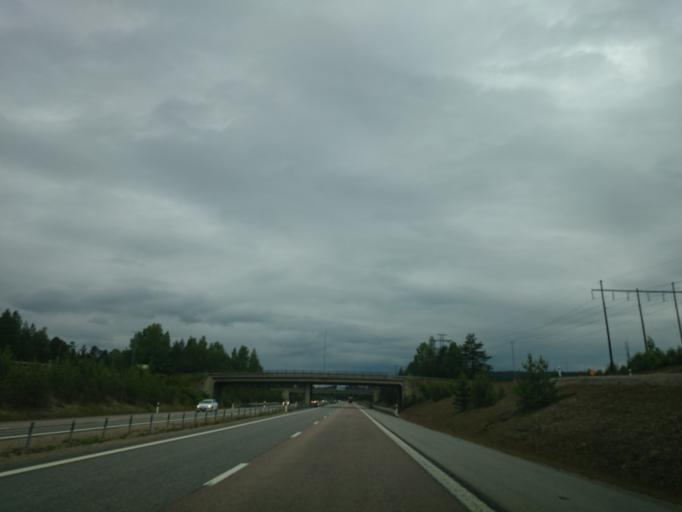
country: SE
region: Vaesternorrland
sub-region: Timra Kommun
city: Timra
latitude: 62.4985
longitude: 17.3398
